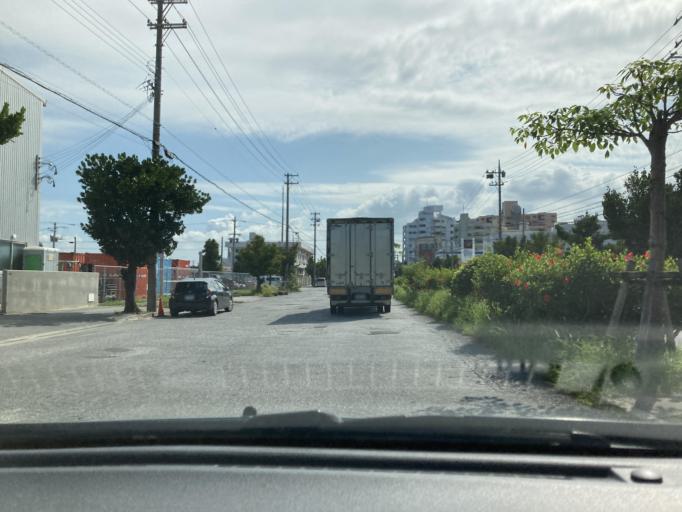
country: JP
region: Okinawa
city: Naha-shi
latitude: 26.2435
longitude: 127.6787
